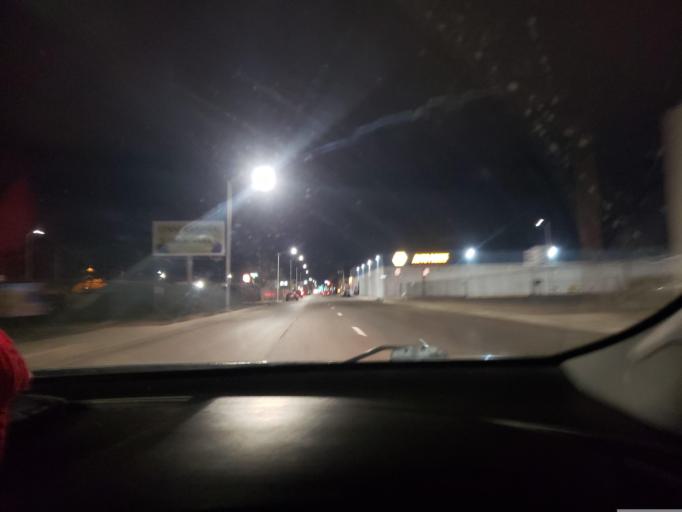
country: US
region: New Mexico
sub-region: Bernalillo County
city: Albuquerque
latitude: 35.0977
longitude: -106.6466
